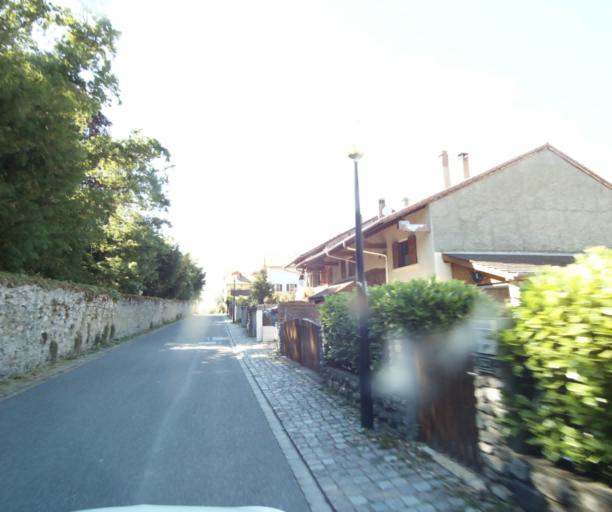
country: FR
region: Rhone-Alpes
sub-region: Departement de la Haute-Savoie
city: Massongy
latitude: 46.3164
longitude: 6.3335
